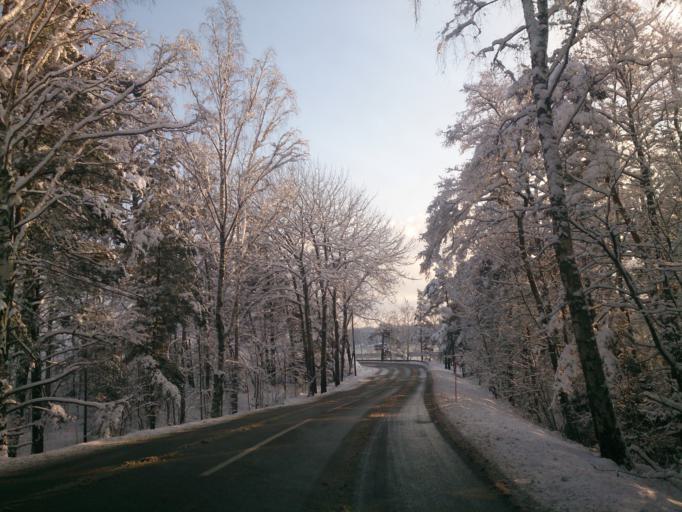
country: SE
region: Stockholm
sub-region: Varmdo Kommun
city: Holo
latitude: 59.2837
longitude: 18.5911
